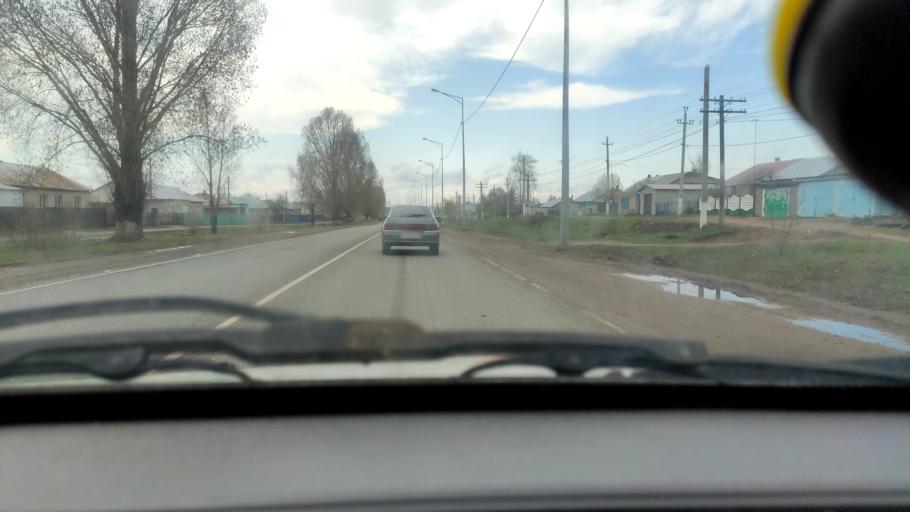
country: RU
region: Samara
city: Zhigulevsk
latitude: 53.5543
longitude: 49.5317
